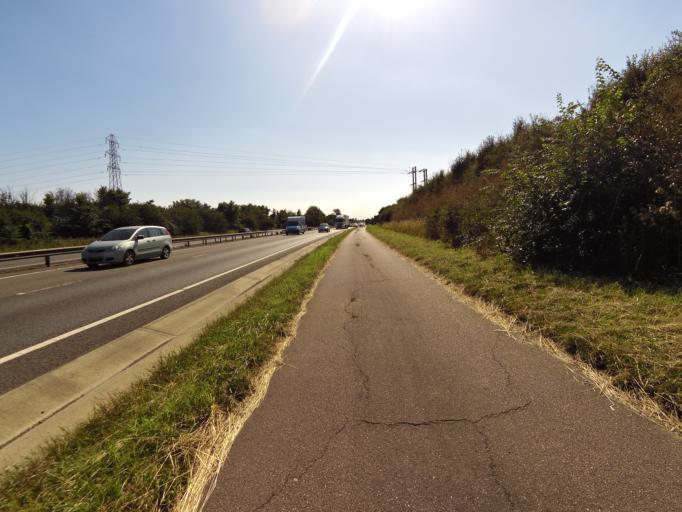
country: GB
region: England
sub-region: Essex
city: Marks Tey
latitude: 51.8561
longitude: 0.7387
